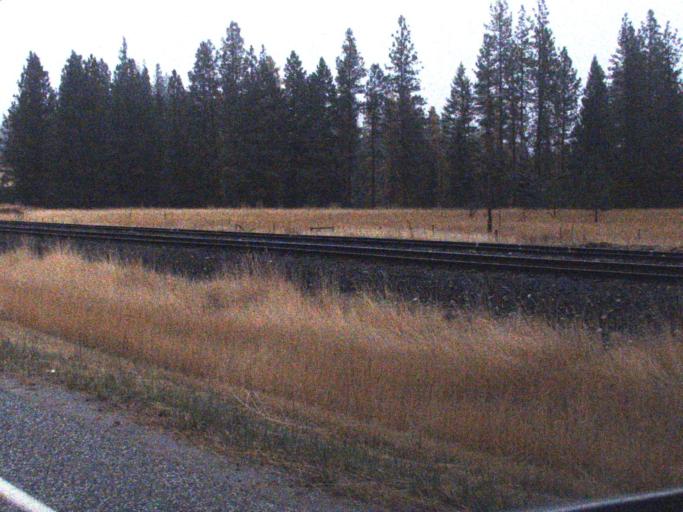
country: US
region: Washington
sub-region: Stevens County
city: Kettle Falls
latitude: 48.7140
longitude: -118.1333
